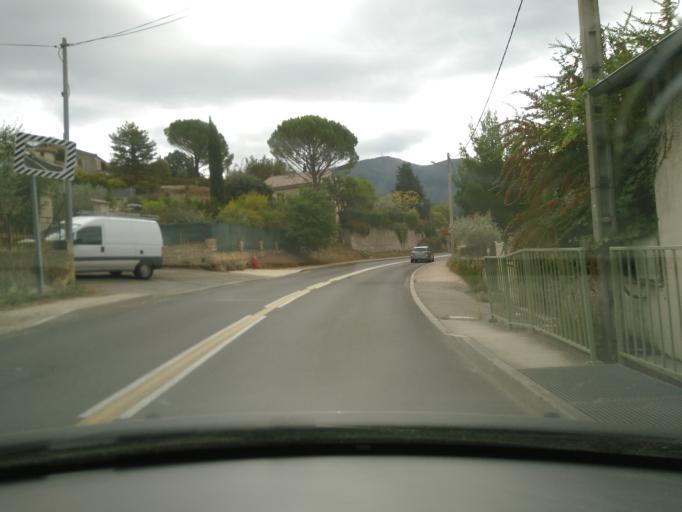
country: FR
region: Rhone-Alpes
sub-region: Departement de la Drome
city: Nyons
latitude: 44.3642
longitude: 5.1268
